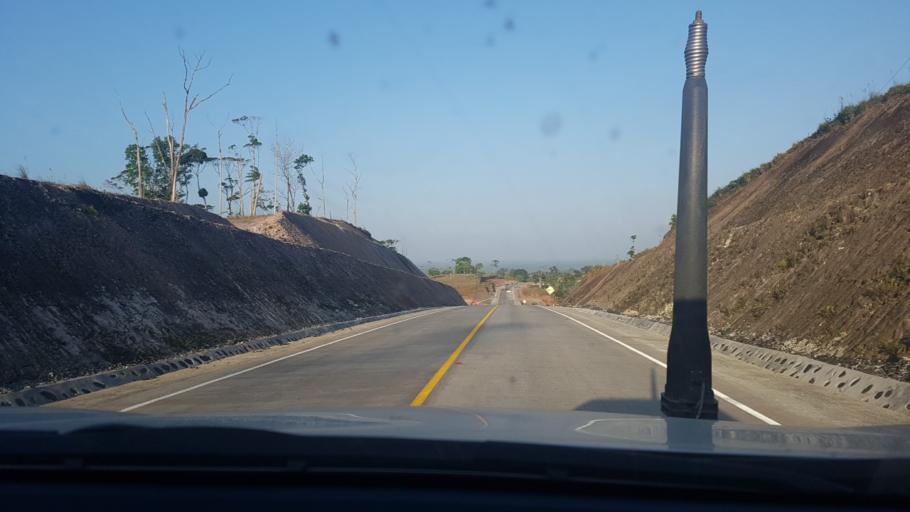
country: NI
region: Atlantico Sur
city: Rama
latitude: 11.8345
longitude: -84.0762
